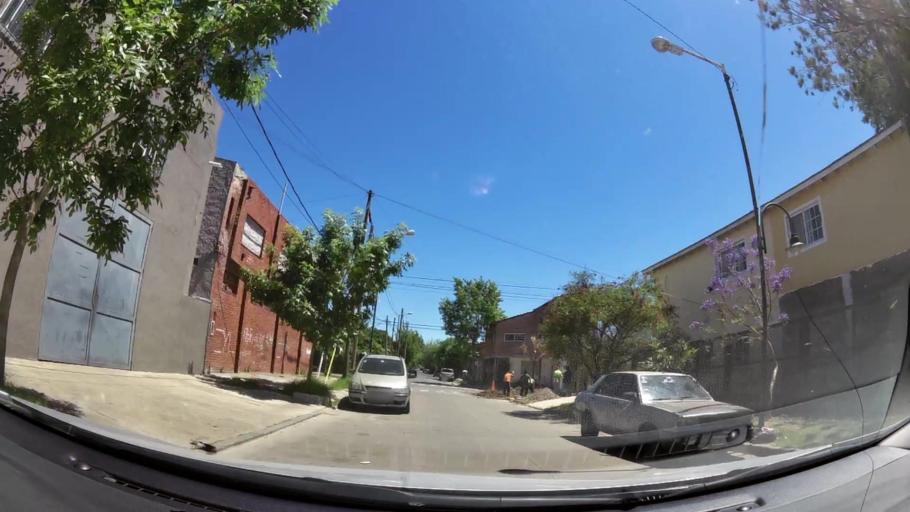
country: AR
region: Buenos Aires
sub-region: Partido de Tigre
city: Tigre
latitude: -34.4565
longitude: -58.5554
